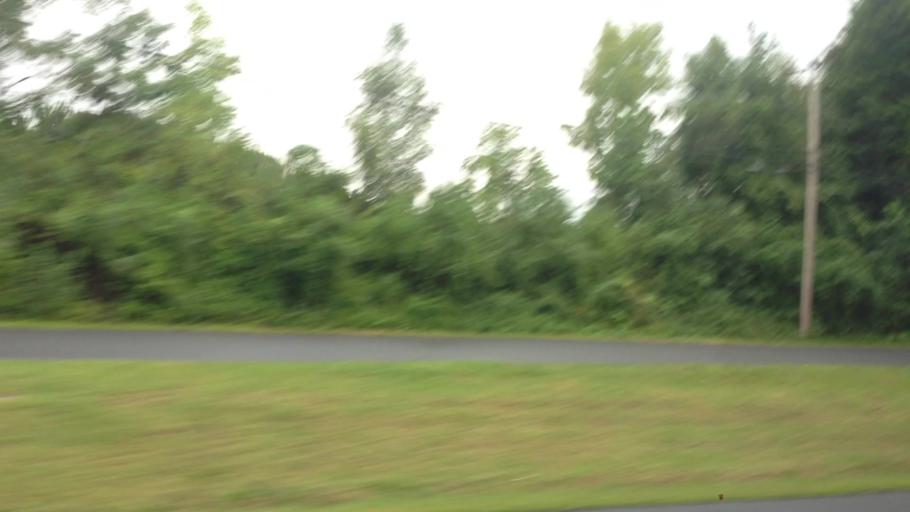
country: US
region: New York
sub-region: Ulster County
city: Lincoln Park
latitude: 41.9544
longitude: -73.9753
